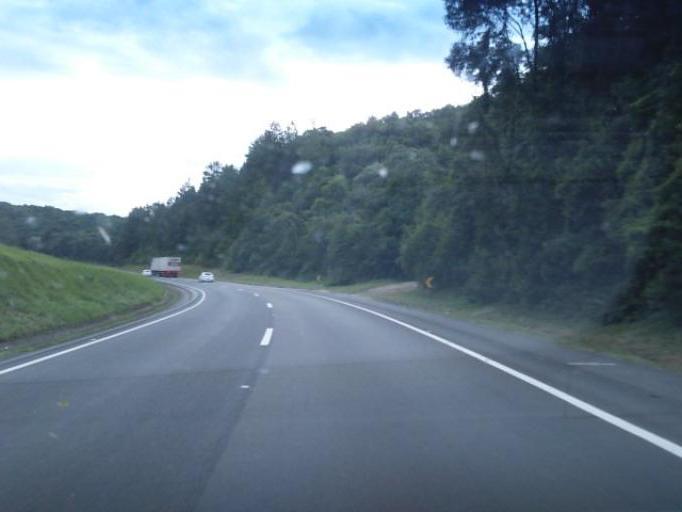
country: BR
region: Parana
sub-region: Campina Grande Do Sul
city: Campina Grande do Sul
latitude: -25.1981
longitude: -48.8944
